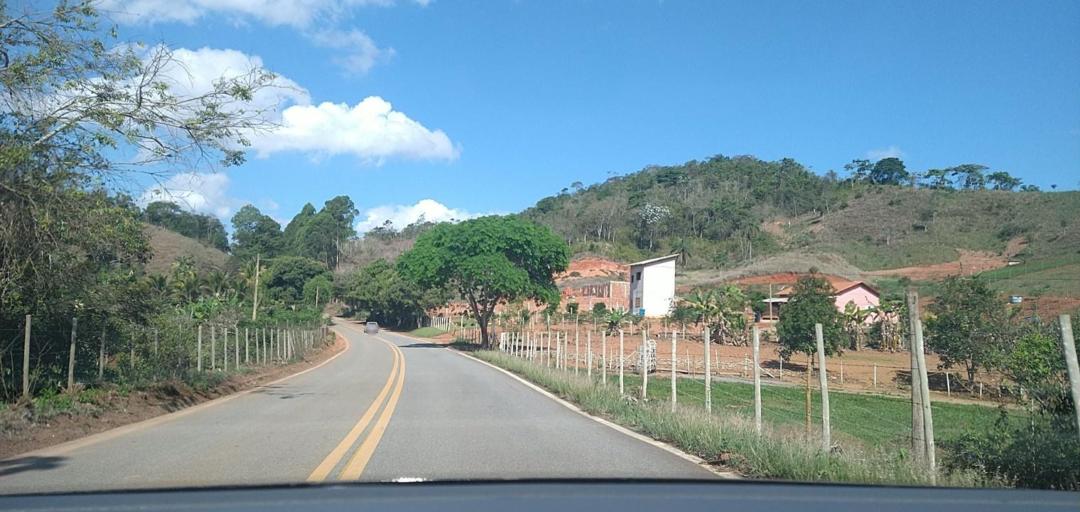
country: BR
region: Minas Gerais
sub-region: Alvinopolis
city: Alvinopolis
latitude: -20.0359
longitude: -43.0417
